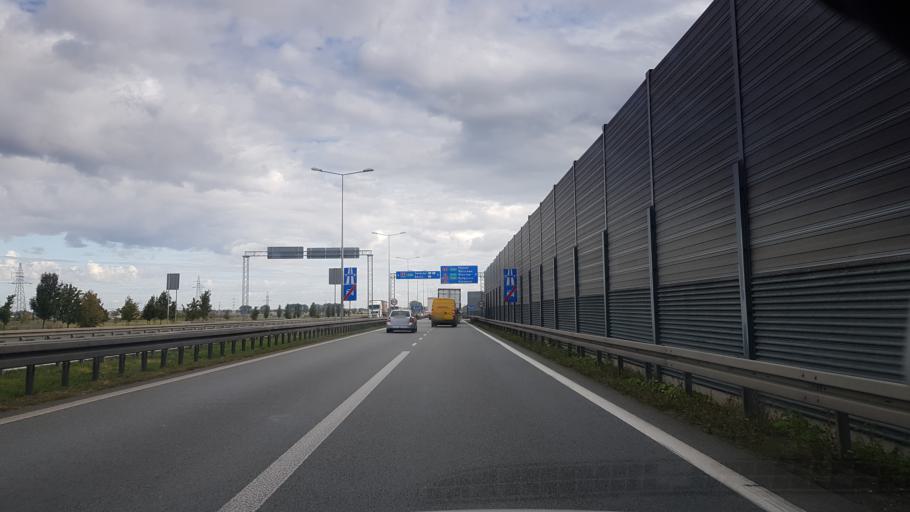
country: PL
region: Greater Poland Voivodeship
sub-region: Powiat poznanski
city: Komorniki
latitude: 52.3463
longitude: 16.7597
